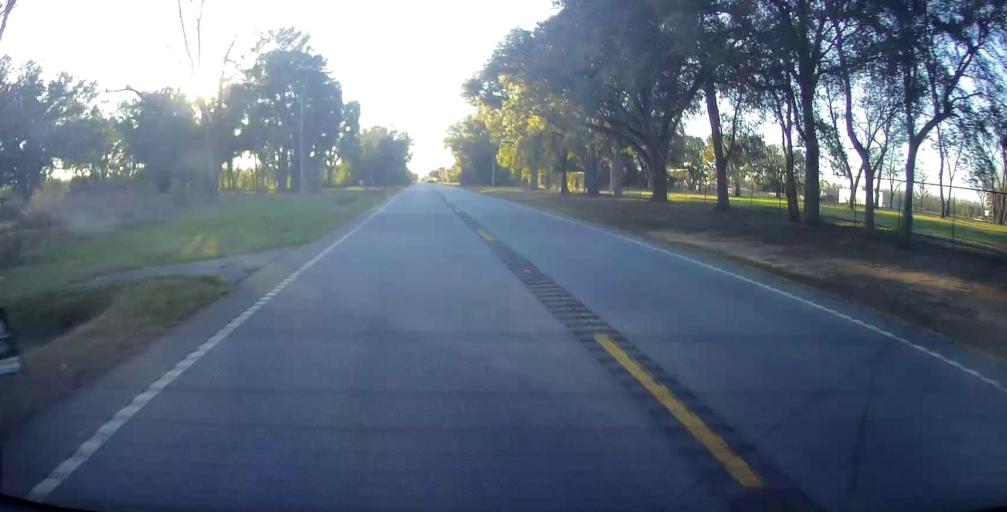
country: US
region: Georgia
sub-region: Dougherty County
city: Albany
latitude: 31.5041
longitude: -84.2351
